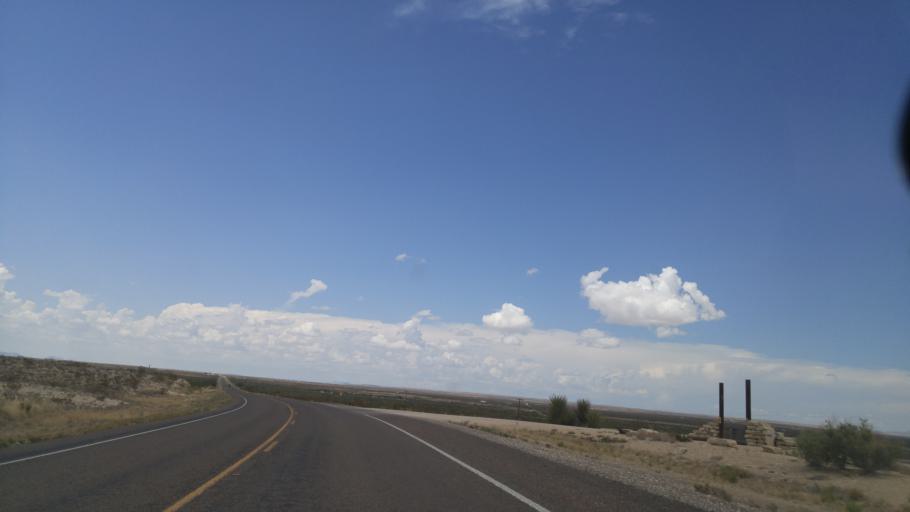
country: US
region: Texas
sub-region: Brewster County
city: Alpine
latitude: 29.5994
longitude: -103.5602
